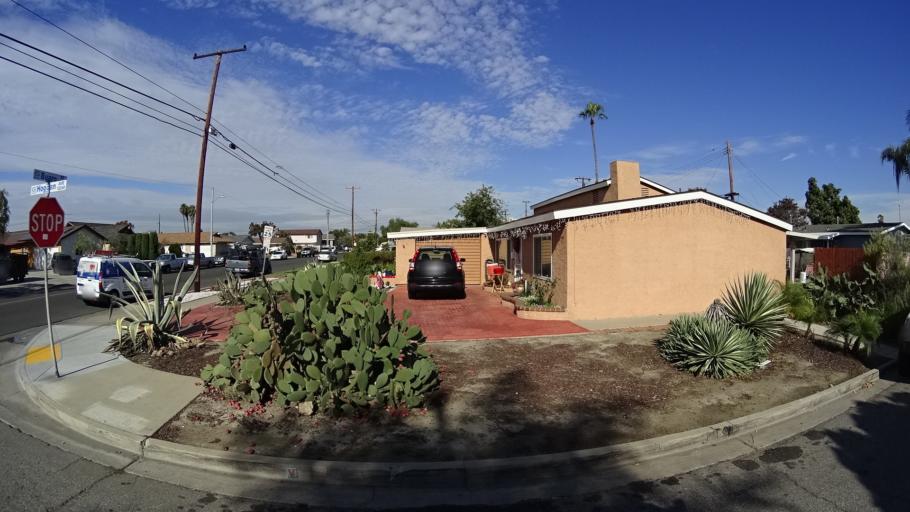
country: US
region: California
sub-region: Orange County
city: Garden Grove
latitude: 33.7824
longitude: -117.9190
